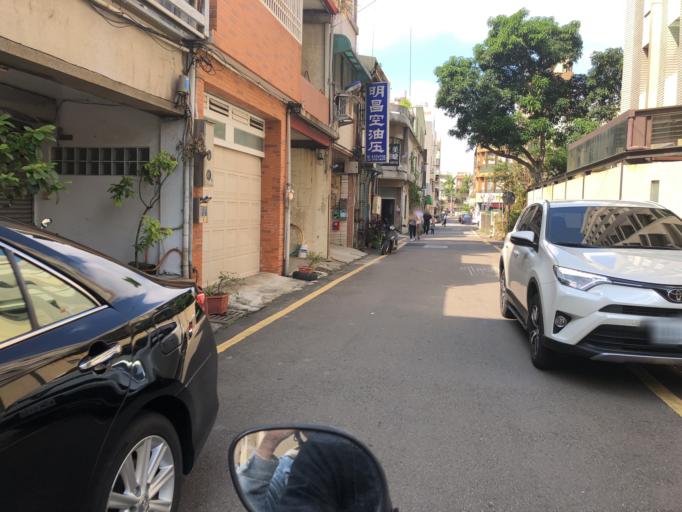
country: TW
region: Taiwan
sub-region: Hsinchu
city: Hsinchu
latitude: 24.8087
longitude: 120.9797
